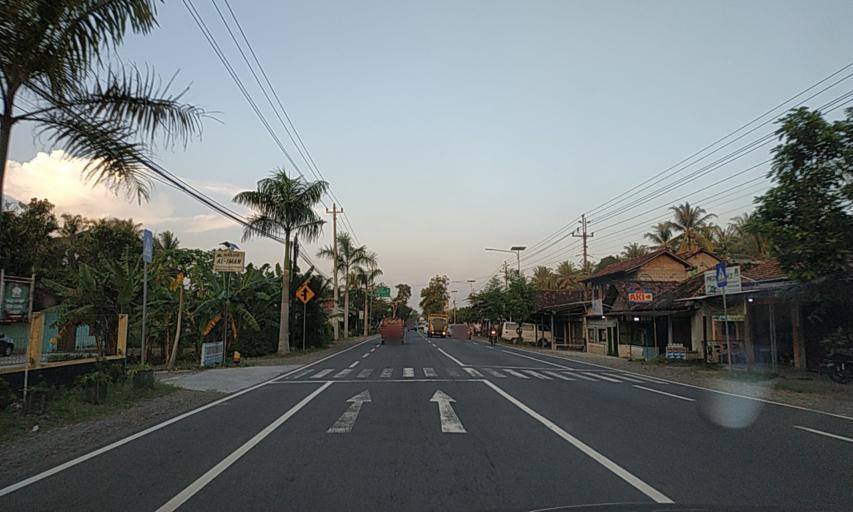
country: ID
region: Daerah Istimewa Yogyakarta
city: Srandakan
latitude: -7.8902
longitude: 110.1075
